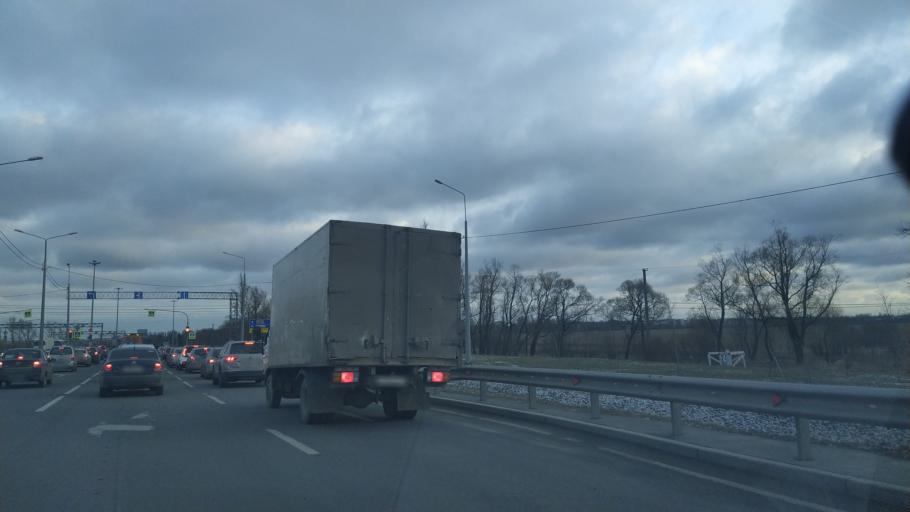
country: RU
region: St.-Petersburg
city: Pushkin
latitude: 59.7537
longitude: 30.3886
